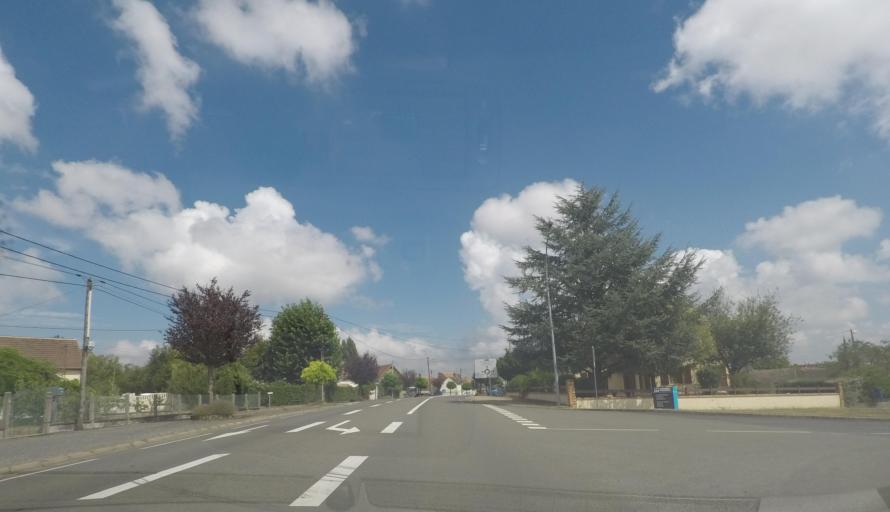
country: FR
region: Pays de la Loire
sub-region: Departement de la Sarthe
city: Saint-Cosme-en-Vairais
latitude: 48.2718
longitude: 0.4539
